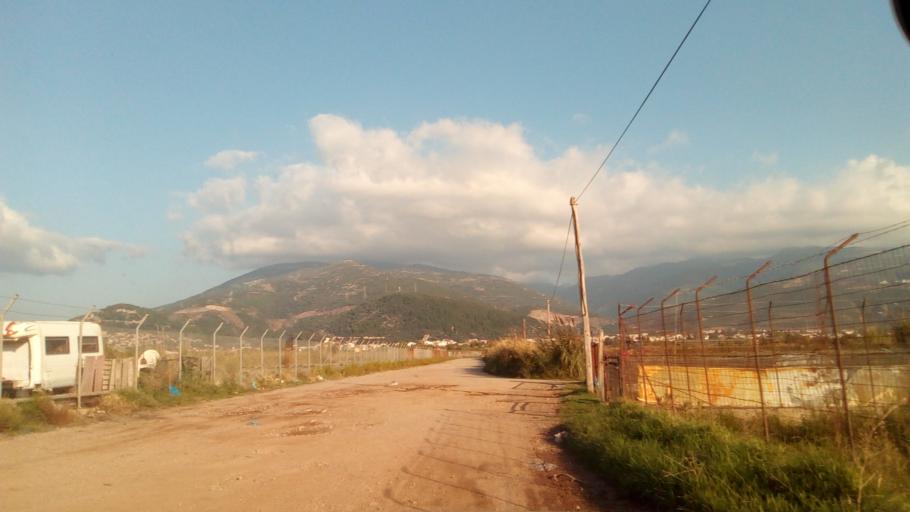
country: GR
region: West Greece
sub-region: Nomos Aitolias kai Akarnanias
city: Nafpaktos
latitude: 38.3807
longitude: 21.8516
